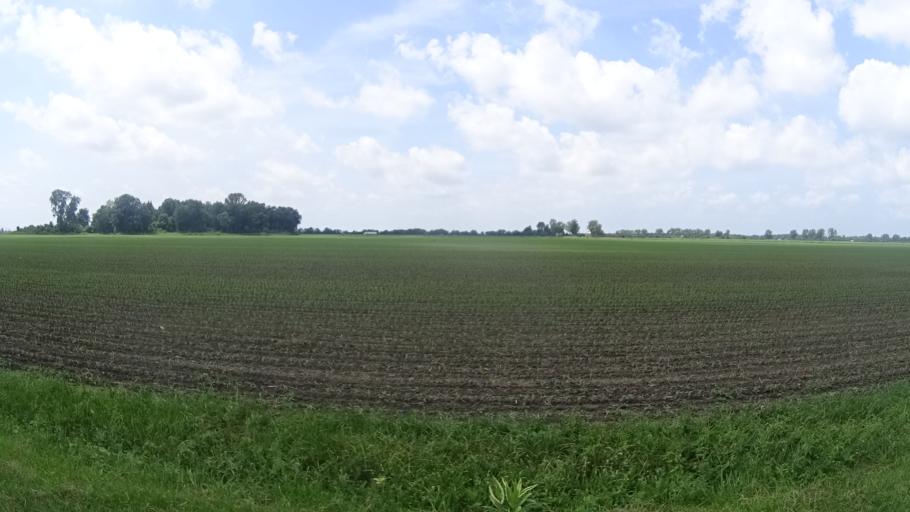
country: US
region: Ohio
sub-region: Huron County
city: Bellevue
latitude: 41.3041
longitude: -82.7657
